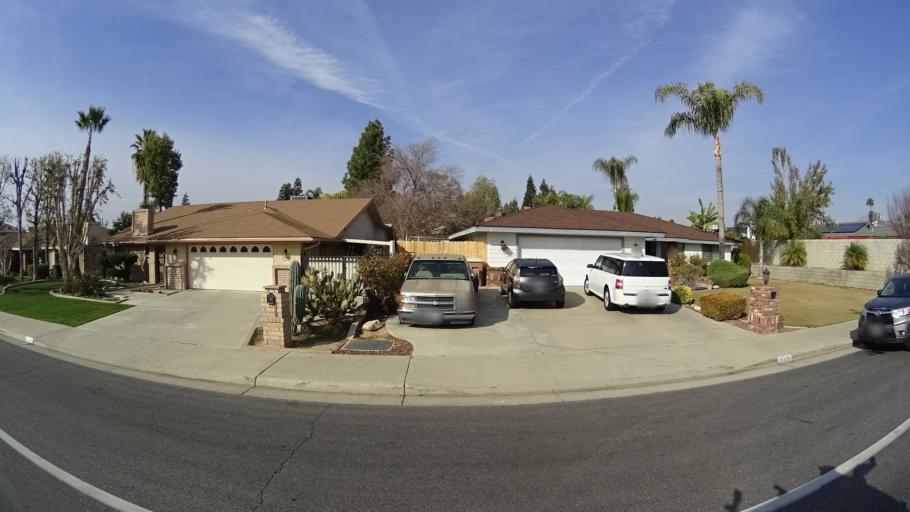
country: US
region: California
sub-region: Kern County
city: Oildale
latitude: 35.4054
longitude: -118.9387
